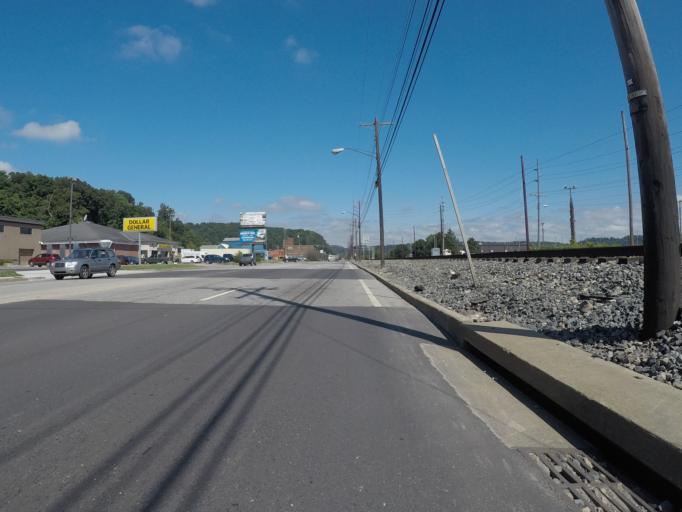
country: US
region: Kentucky
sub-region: Boyd County
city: Ashland
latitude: 38.4499
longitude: -82.6122
